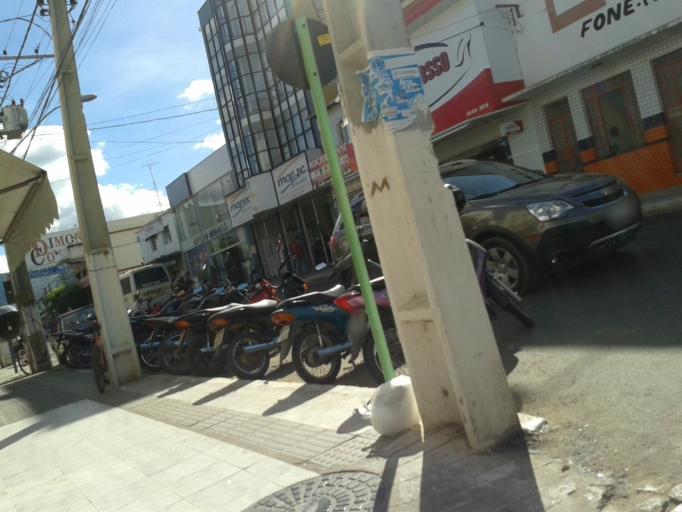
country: BR
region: Bahia
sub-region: Livramento Do Brumado
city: Livramento do Brumado
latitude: -13.6498
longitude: -41.8424
